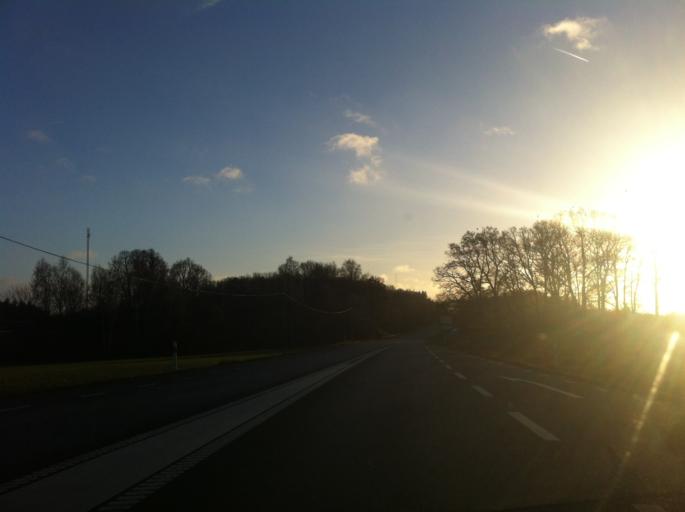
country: SE
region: Skane
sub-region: Hassleholms Kommun
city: Hassleholm
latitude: 56.1260
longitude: 13.7987
